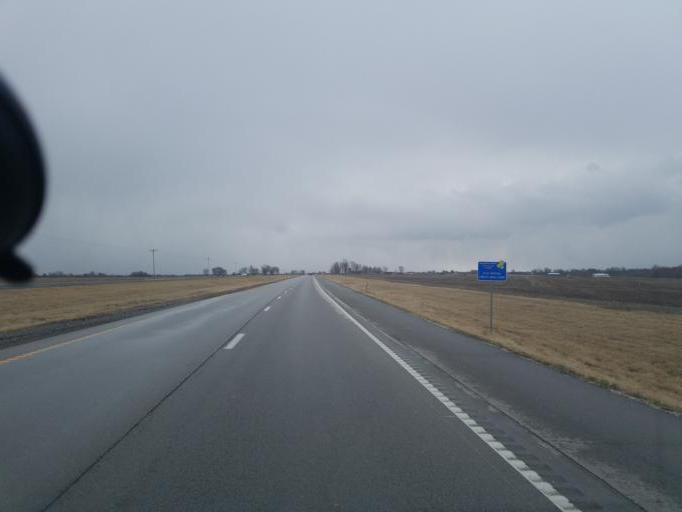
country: US
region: Missouri
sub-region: Macon County
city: Macon
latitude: 39.8315
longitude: -92.4750
